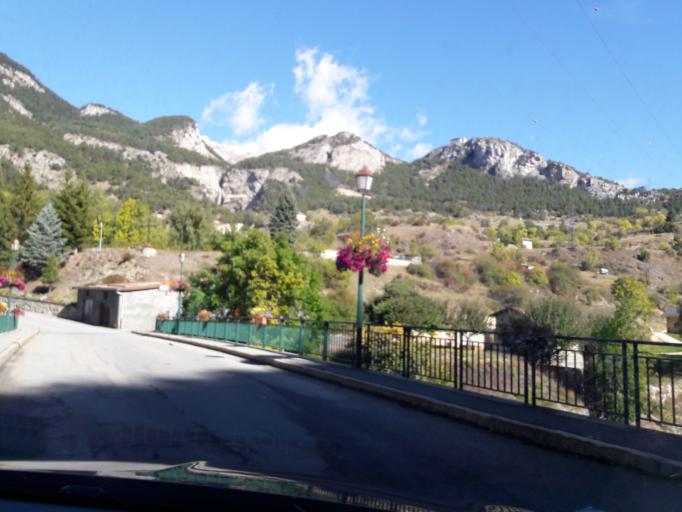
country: FR
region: Rhone-Alpes
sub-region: Departement de la Savoie
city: Modane
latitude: 45.2131
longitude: 6.7234
